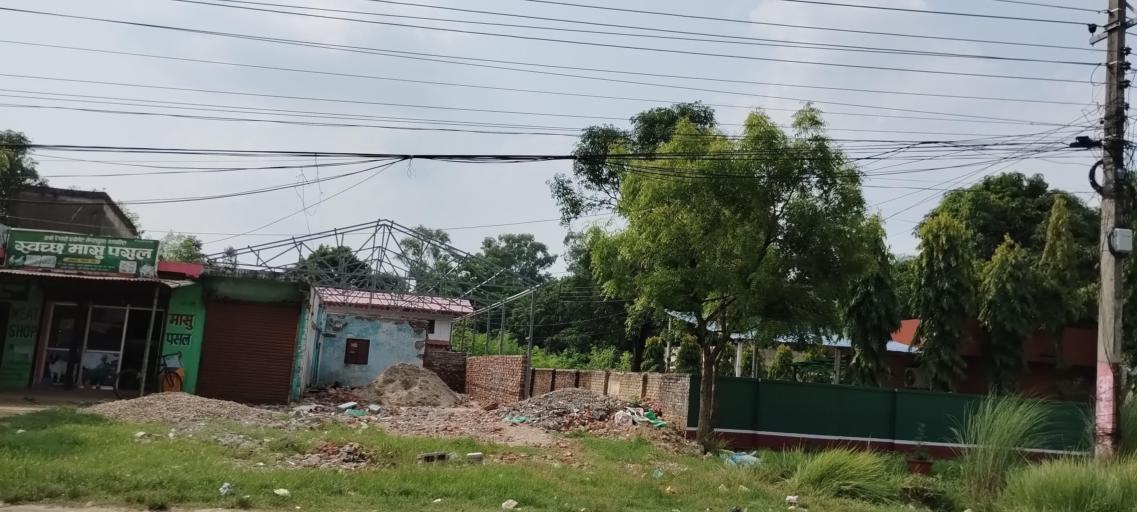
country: NP
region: Mid Western
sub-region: Bheri Zone
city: Nepalgunj
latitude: 28.1628
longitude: 81.6725
